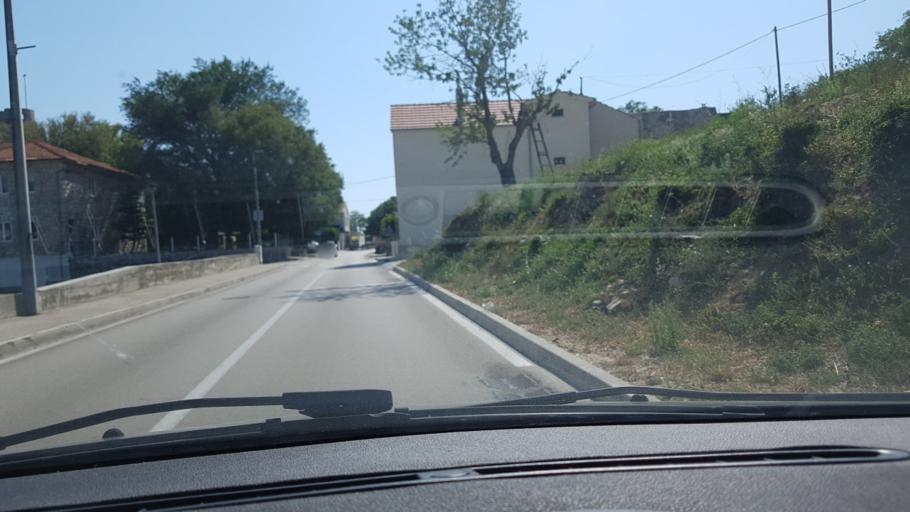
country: HR
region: Splitsko-Dalmatinska
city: Klis
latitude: 43.5617
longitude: 16.5236
